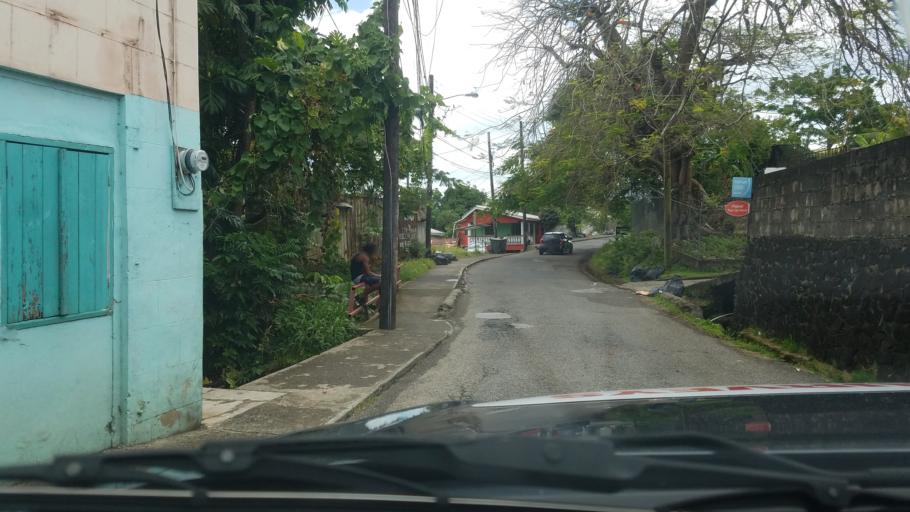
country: LC
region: Castries Quarter
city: Bisee
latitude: 14.0045
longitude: -60.9829
